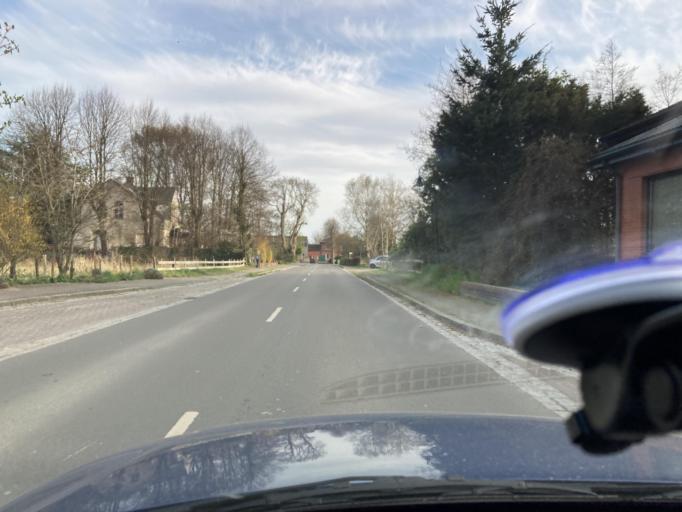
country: DE
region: Schleswig-Holstein
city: Schulp
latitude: 54.2447
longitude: 8.9371
